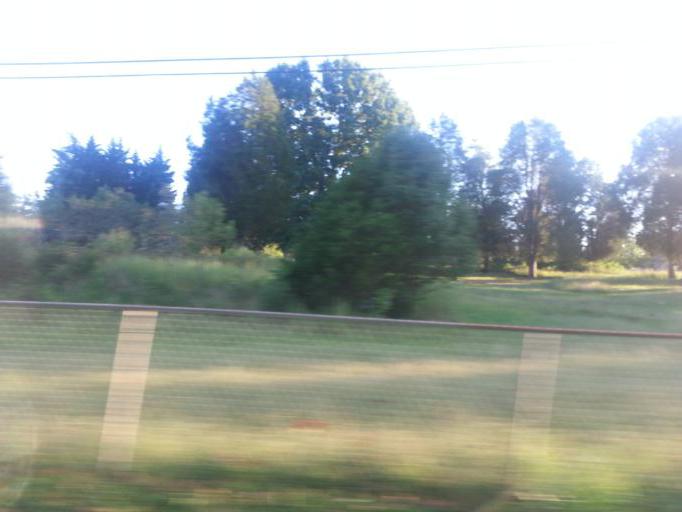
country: US
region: Tennessee
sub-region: Blount County
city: Wildwood
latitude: 35.8936
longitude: -83.8506
